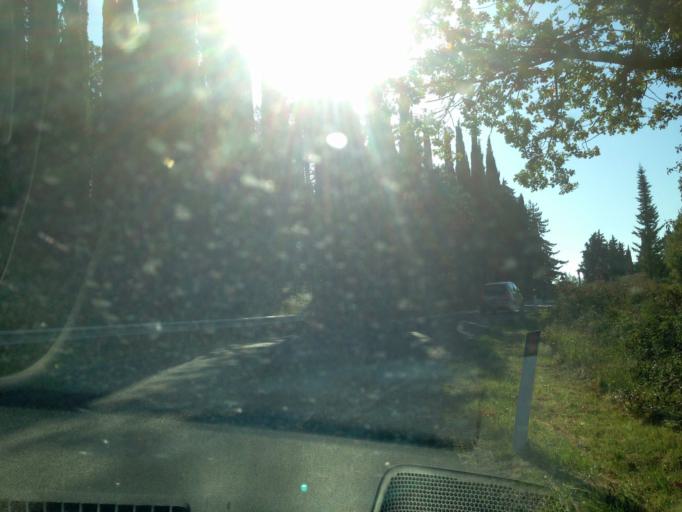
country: IT
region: Tuscany
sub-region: Provincia di Siena
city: Castellina in Chianti
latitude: 43.4408
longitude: 11.3007
